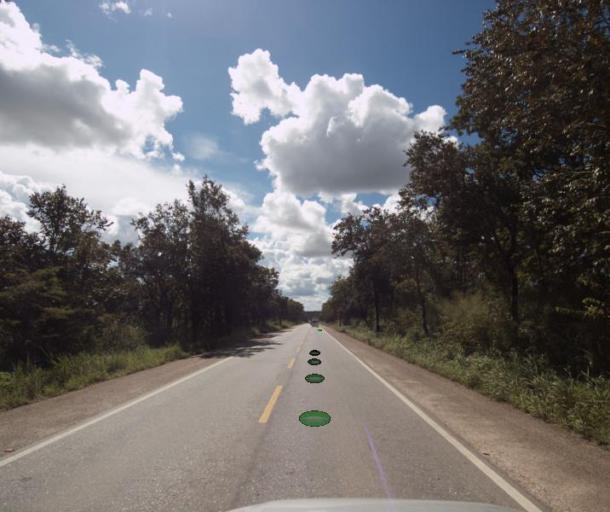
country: BR
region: Goias
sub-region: Porangatu
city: Porangatu
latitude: -13.6591
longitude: -49.0345
